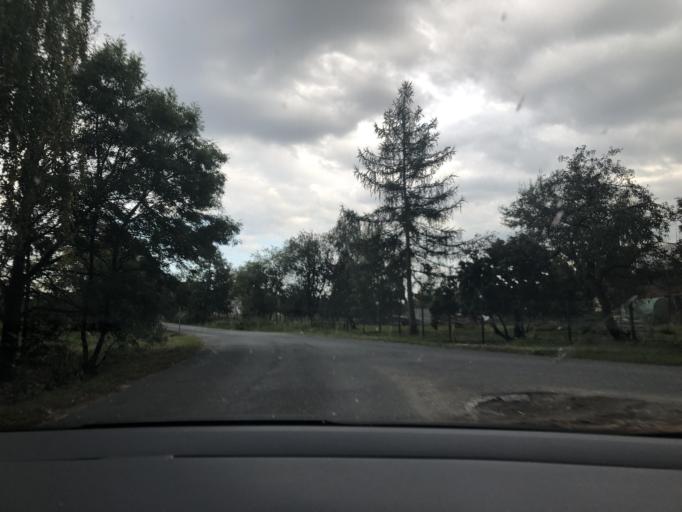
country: CZ
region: Central Bohemia
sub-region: Okres Kolin
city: Tynec nad Labem
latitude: 50.0329
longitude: 15.3526
